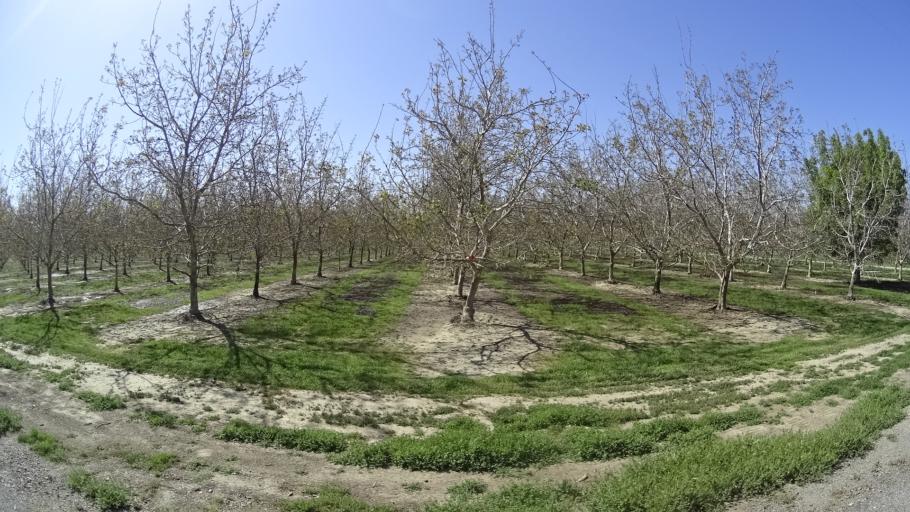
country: US
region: California
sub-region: Glenn County
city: Hamilton City
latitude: 39.7215
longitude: -122.0208
